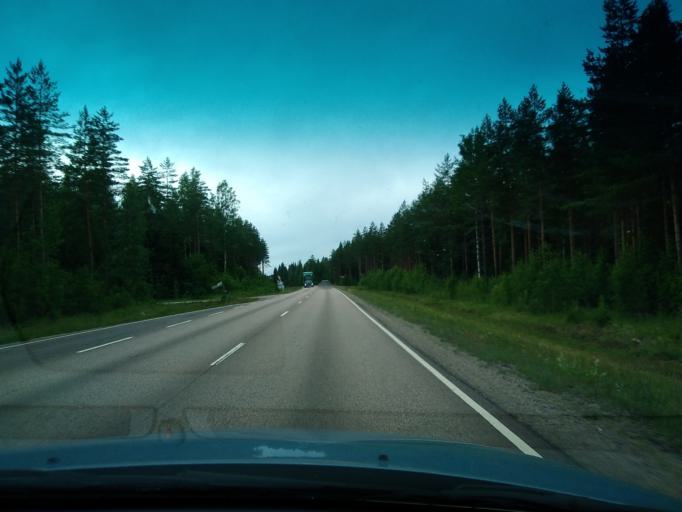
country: FI
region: Central Finland
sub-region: Keuruu
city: Multia
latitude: 62.3795
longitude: 24.7478
